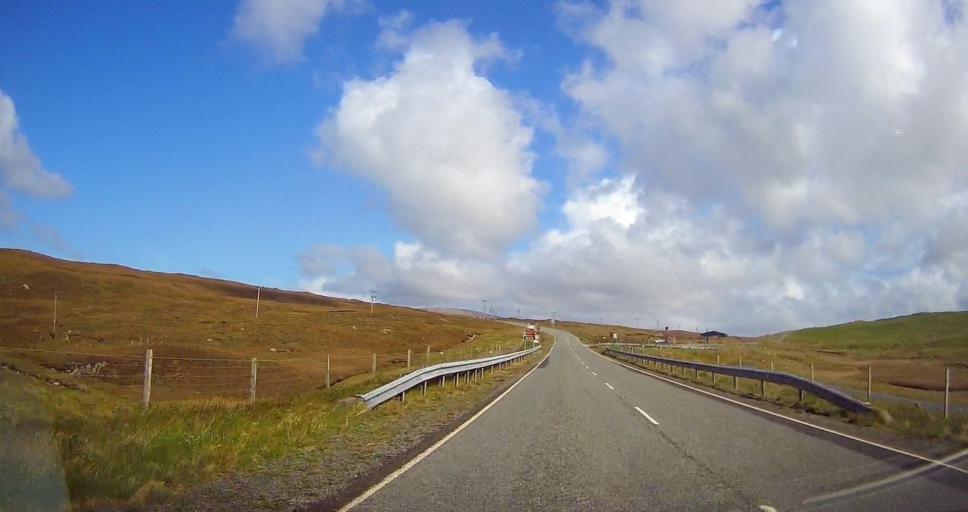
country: GB
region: Scotland
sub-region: Shetland Islands
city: Lerwick
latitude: 60.4745
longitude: -1.4076
